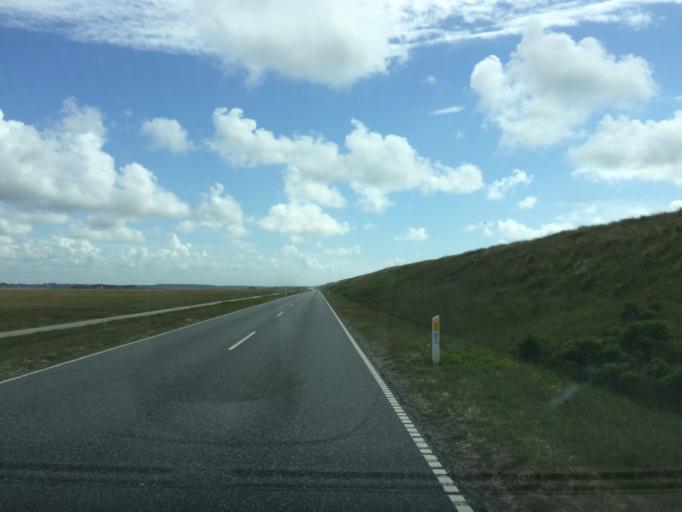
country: DK
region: Central Jutland
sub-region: Holstebro Kommune
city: Ulfborg
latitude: 56.3488
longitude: 8.1224
